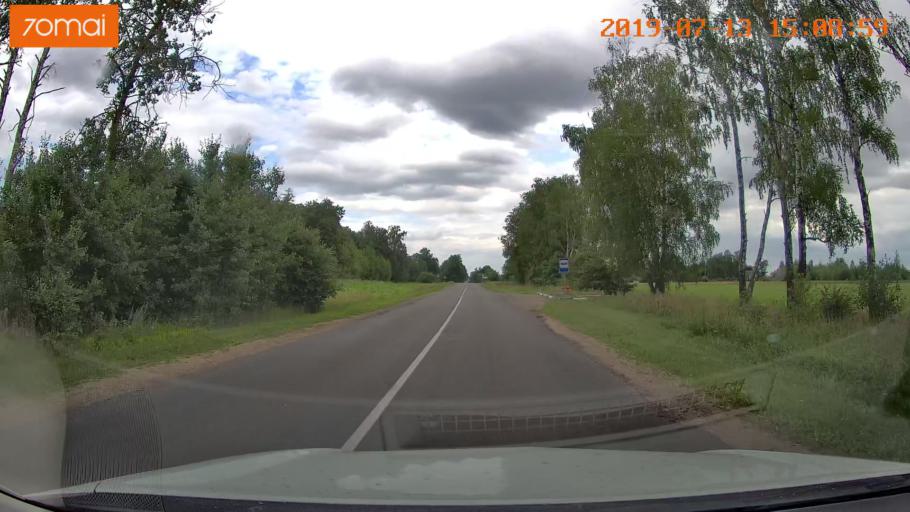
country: BY
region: Mogilev
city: Hlusha
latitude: 53.1746
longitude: 28.7549
